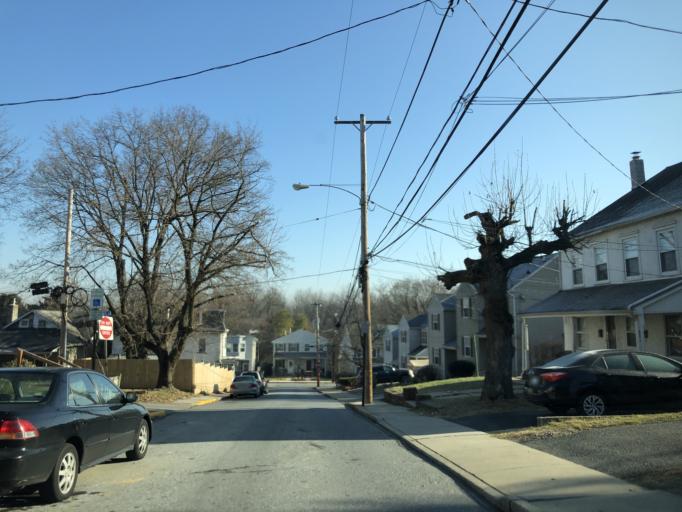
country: US
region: Pennsylvania
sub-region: Chester County
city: Downingtown
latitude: 39.9986
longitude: -75.7112
